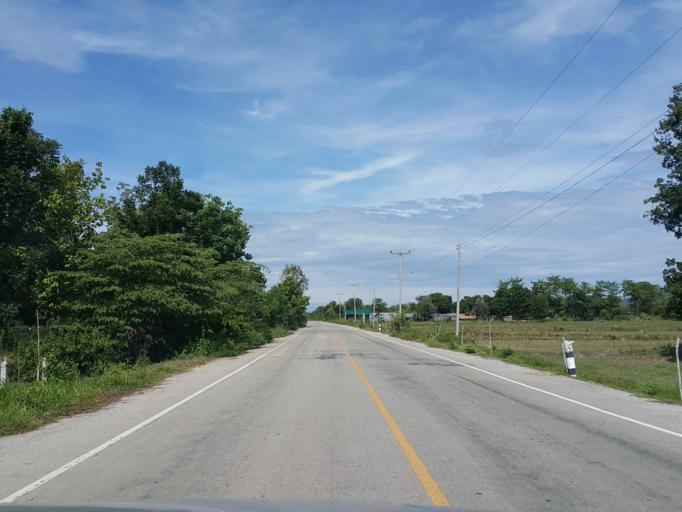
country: TH
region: Sukhothai
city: Ban Dan Lan Hoi
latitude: 17.1153
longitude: 99.5200
